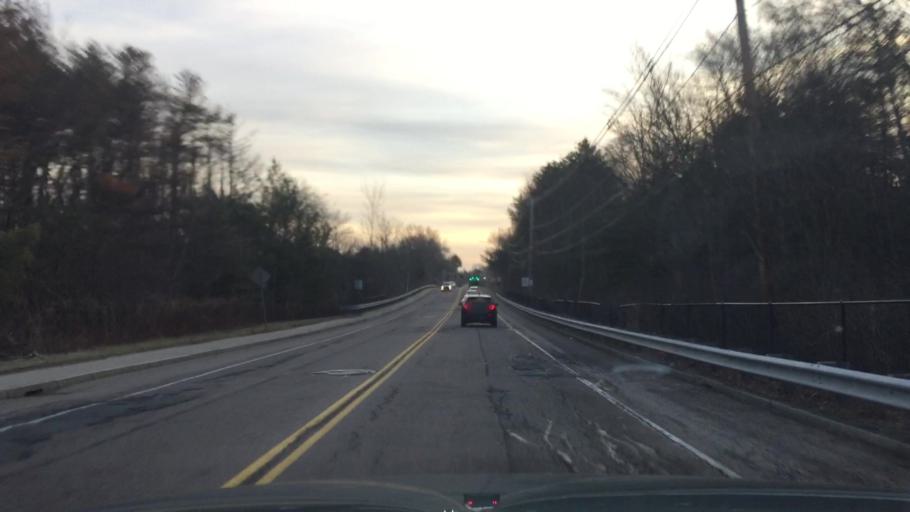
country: US
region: Massachusetts
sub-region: Norfolk County
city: Millis
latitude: 42.1613
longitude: -71.3746
